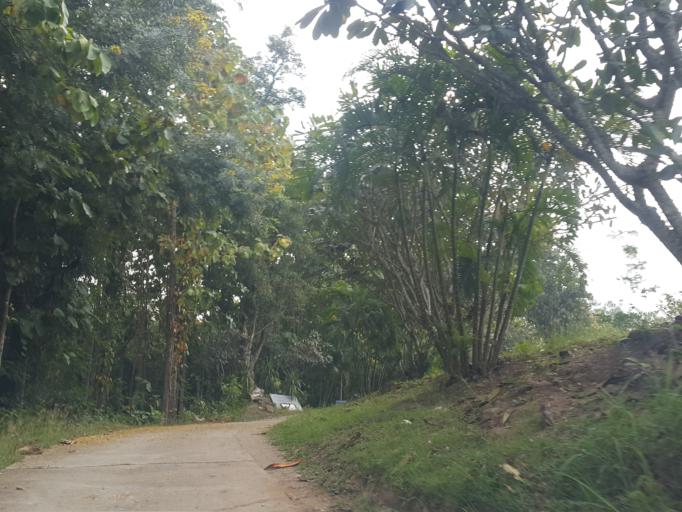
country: TH
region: Chiang Mai
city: Pai
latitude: 19.3601
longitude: 98.4491
